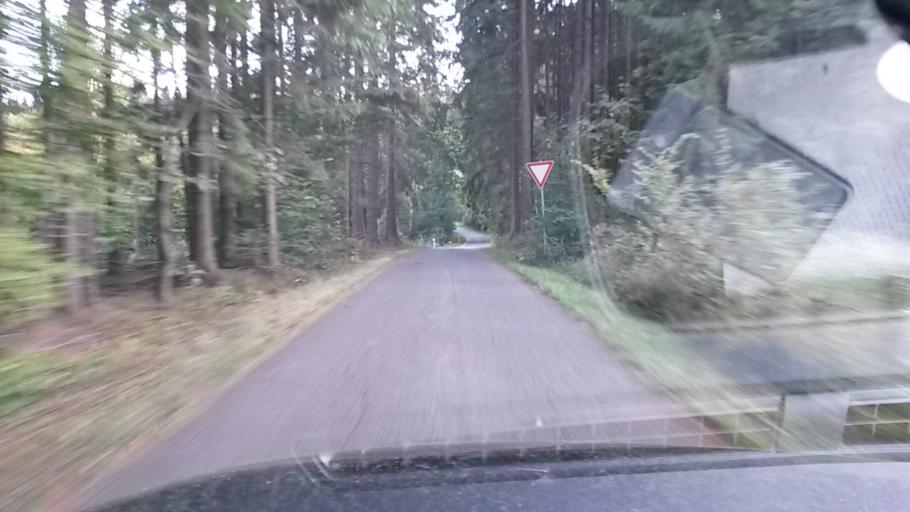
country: DE
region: North Rhine-Westphalia
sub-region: Regierungsbezirk Arnsberg
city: Herscheid
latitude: 51.2028
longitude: 7.7558
